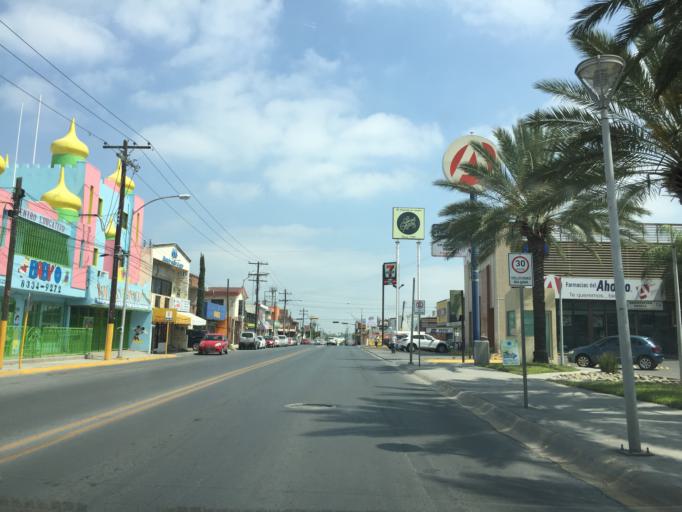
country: MX
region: Nuevo Leon
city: Guadalupe
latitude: 25.7056
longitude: -100.2308
